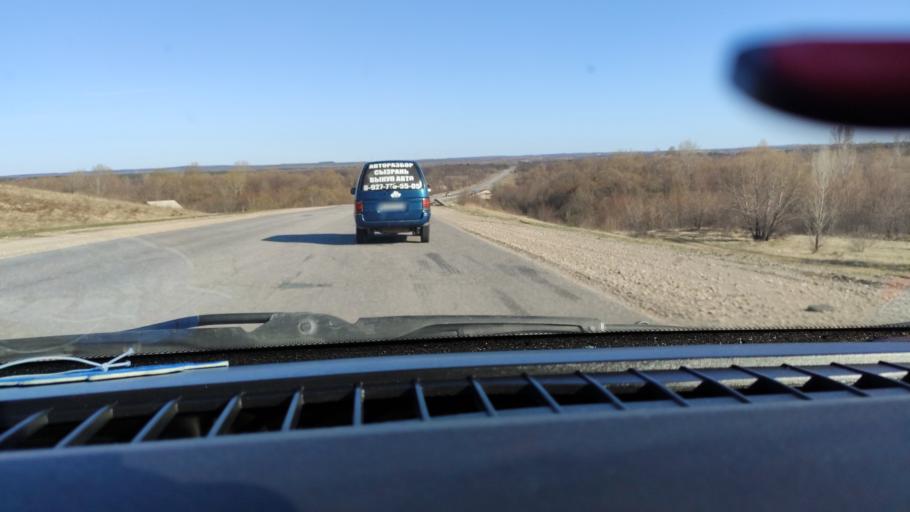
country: RU
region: Samara
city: Varlamovo
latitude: 53.1298
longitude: 48.2881
